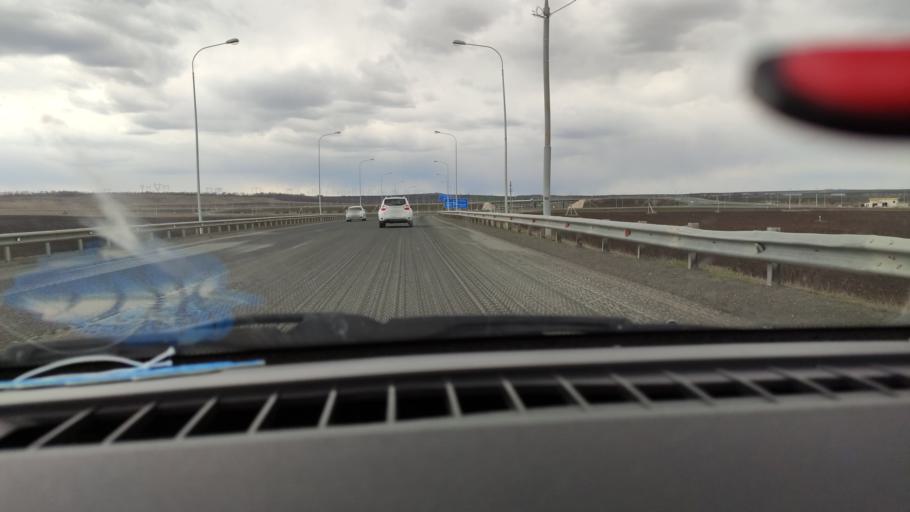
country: RU
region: Saratov
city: Yelshanka
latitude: 51.7977
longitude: 46.1802
